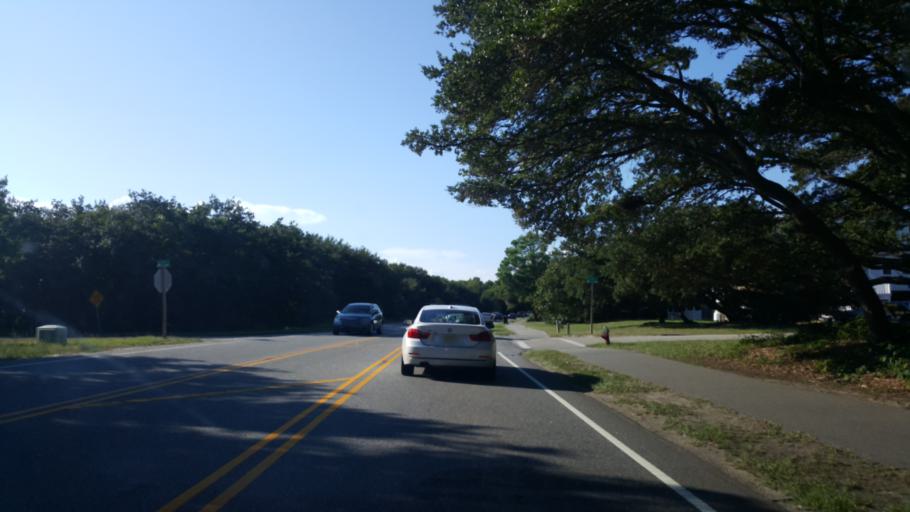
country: US
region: North Carolina
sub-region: Dare County
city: Southern Shores
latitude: 36.1450
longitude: -75.7403
